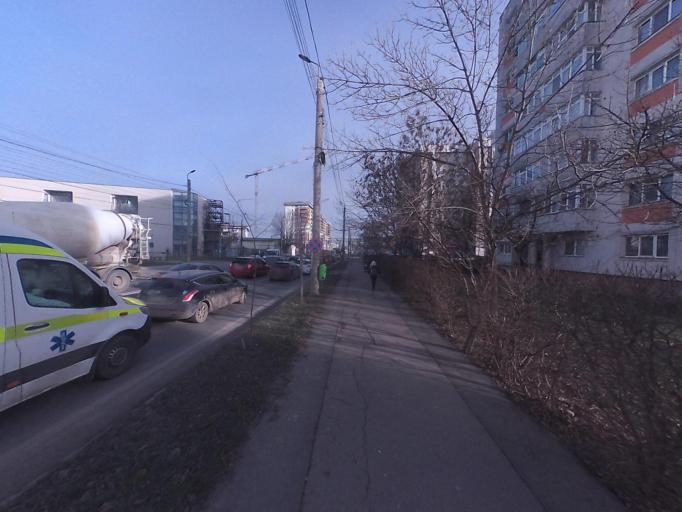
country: RO
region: Iasi
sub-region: Municipiul Iasi
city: Iasi
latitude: 47.1366
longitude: 27.5987
